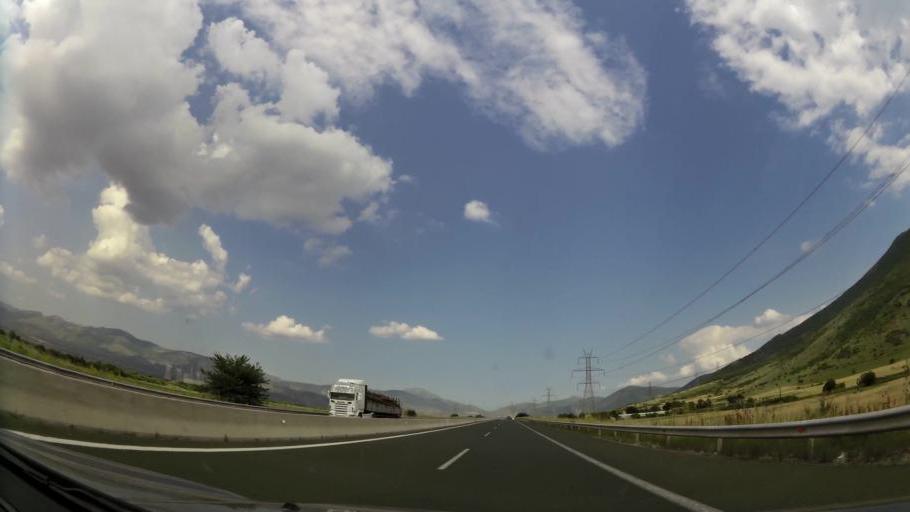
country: GR
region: West Macedonia
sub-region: Nomos Kozanis
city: Kleitos
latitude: 40.3699
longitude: 21.8841
